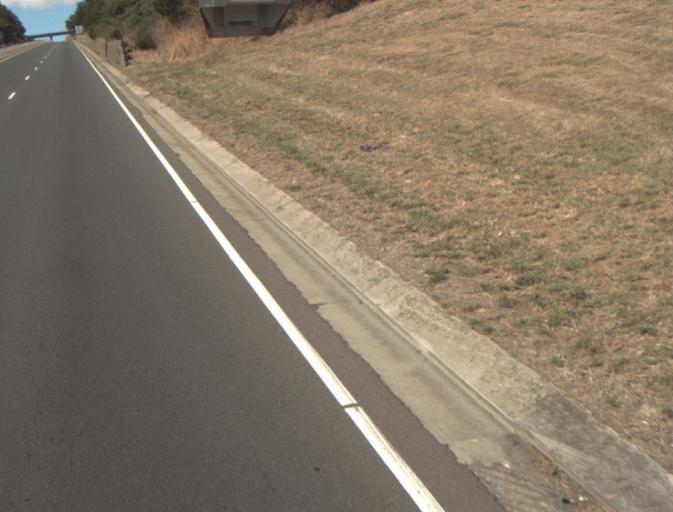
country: AU
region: Tasmania
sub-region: Launceston
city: West Launceston
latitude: -41.4601
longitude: 147.1427
